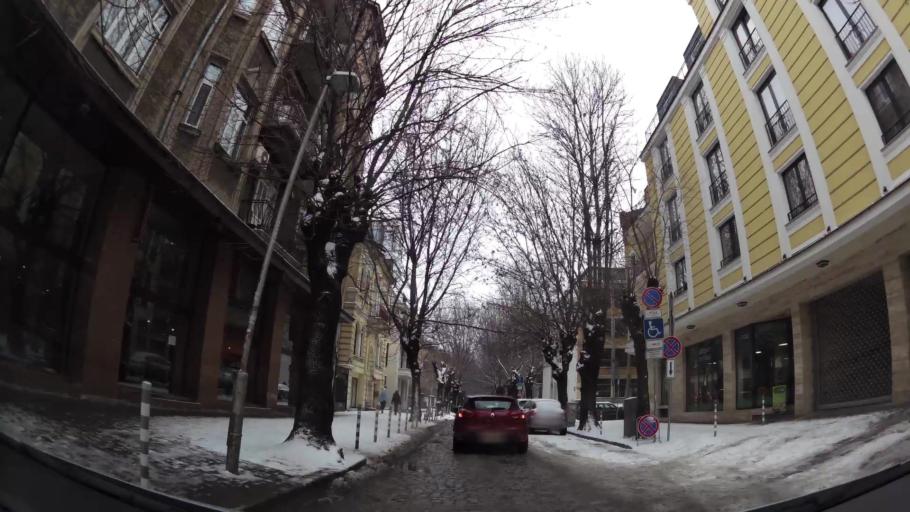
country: BG
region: Sofia-Capital
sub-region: Stolichna Obshtina
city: Sofia
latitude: 42.7000
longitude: 23.3296
